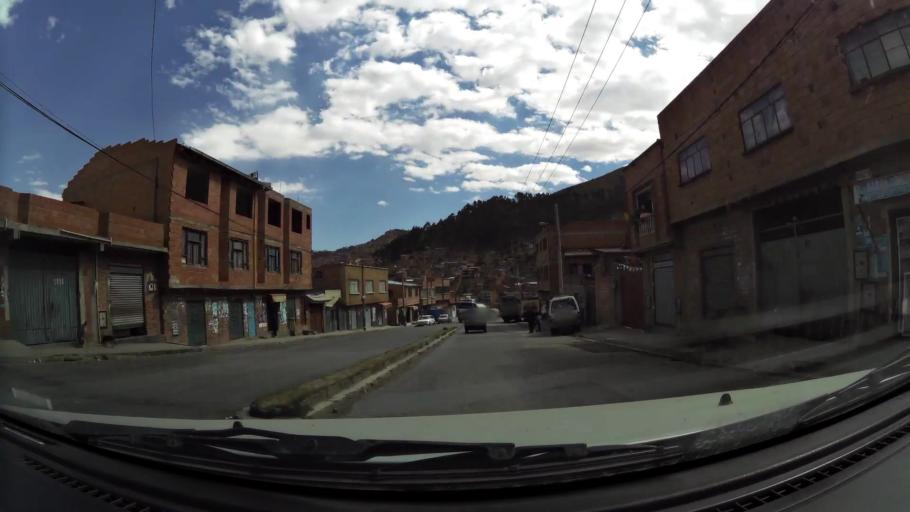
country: BO
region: La Paz
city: La Paz
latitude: -16.4656
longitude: -68.1157
